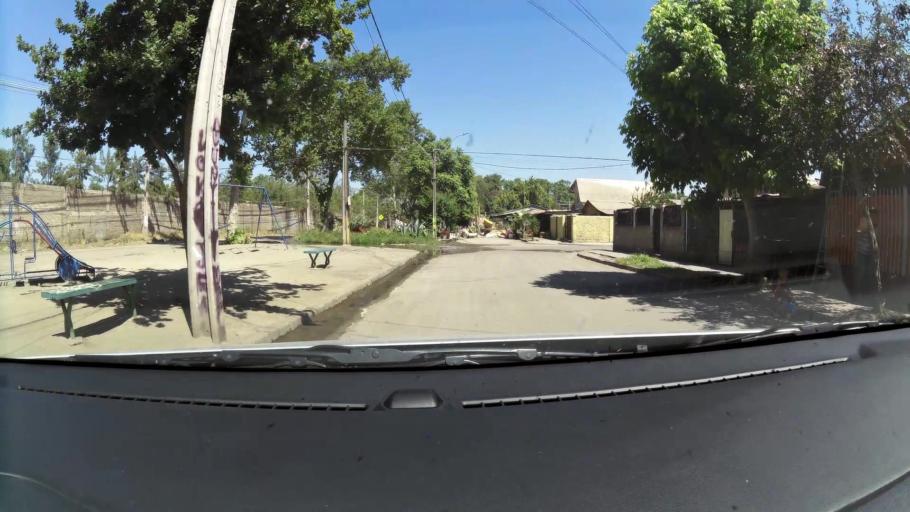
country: CL
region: Santiago Metropolitan
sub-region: Provincia de Maipo
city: San Bernardo
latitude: -33.6274
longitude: -70.7006
